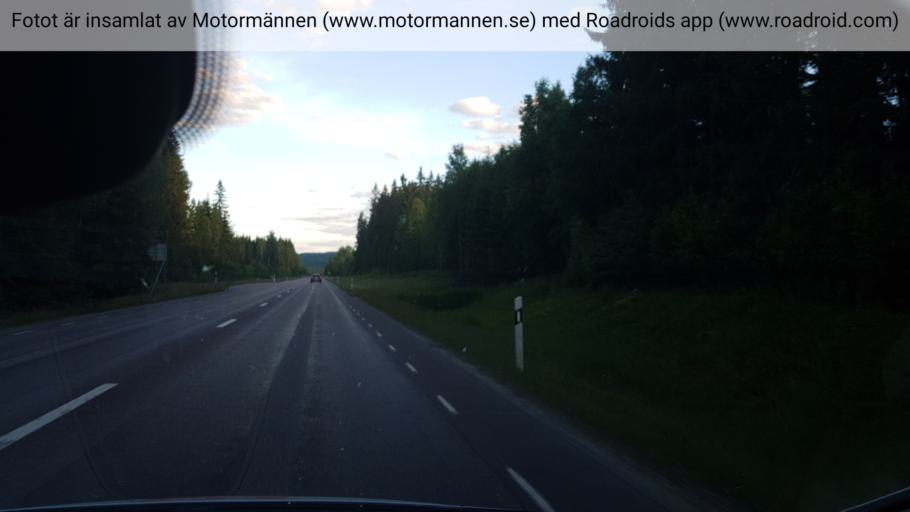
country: SE
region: Vaermland
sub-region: Torsby Kommun
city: Torsby
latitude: 60.1085
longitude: 13.0190
